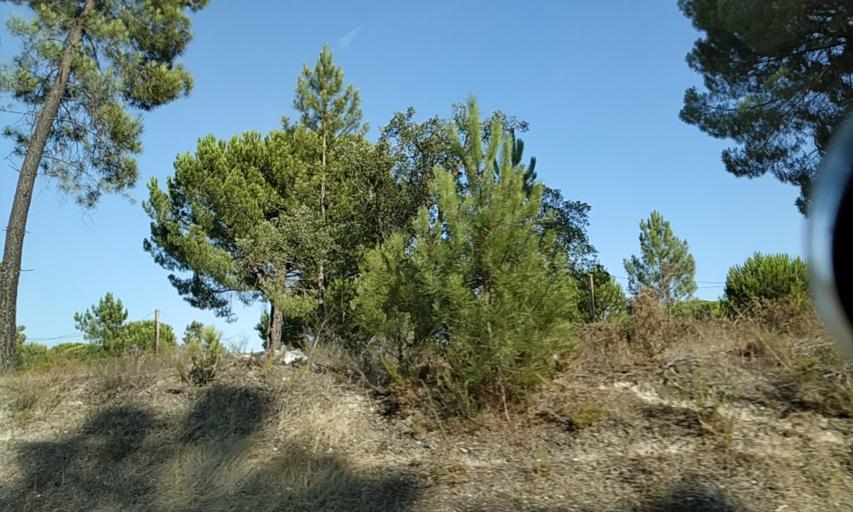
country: PT
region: Santarem
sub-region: Coruche
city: Coruche
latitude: 38.9010
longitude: -8.5305
